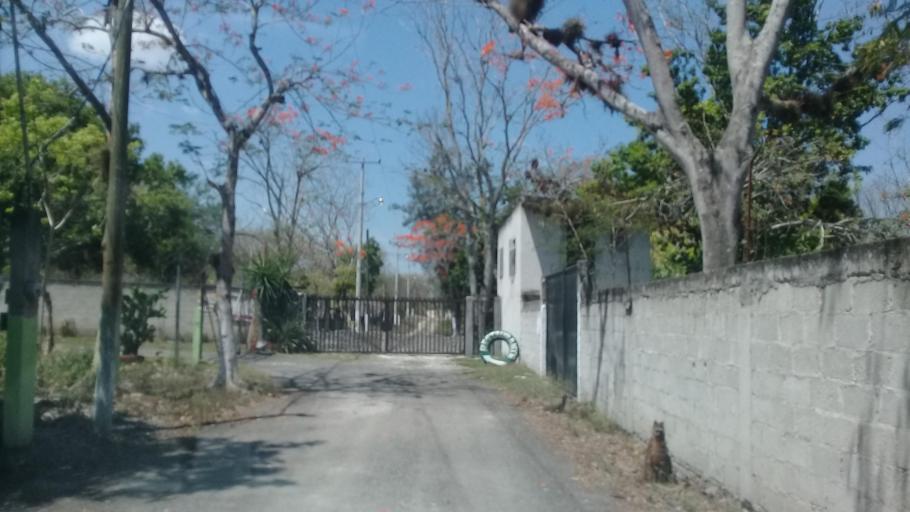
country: MX
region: Veracruz
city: Rinconada
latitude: 19.3796
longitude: -96.5994
